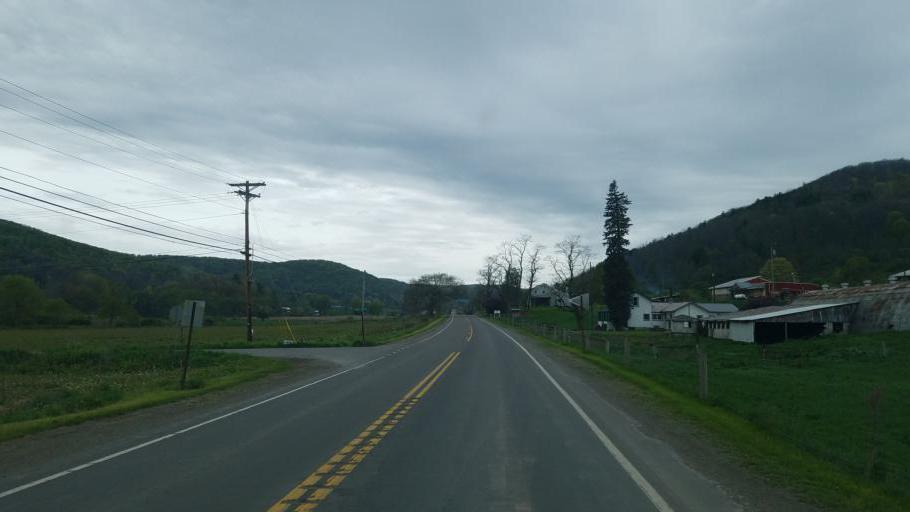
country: US
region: Pennsylvania
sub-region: Tioga County
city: Westfield
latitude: 41.9169
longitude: -77.5708
